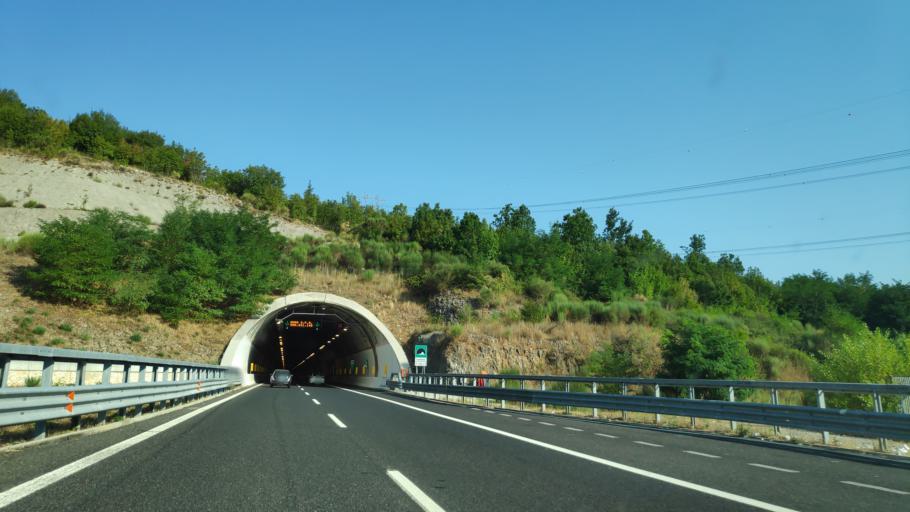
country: IT
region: Campania
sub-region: Provincia di Salerno
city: Casalbuono
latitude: 40.2009
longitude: 15.6868
